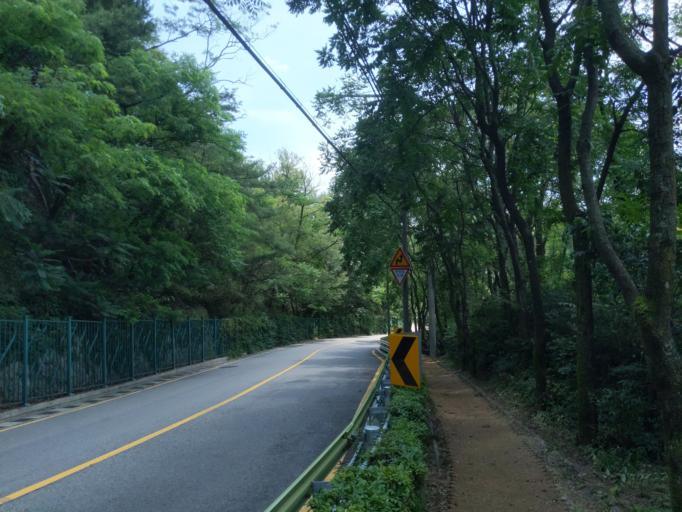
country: KR
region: Seoul
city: Seoul
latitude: 37.5992
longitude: 126.9730
